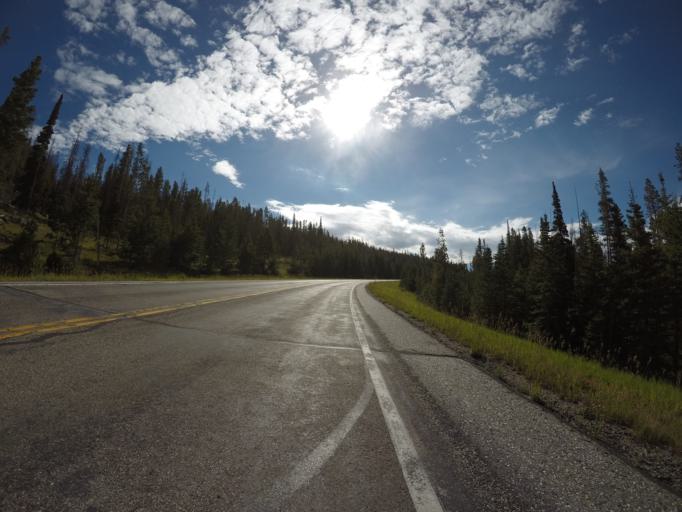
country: US
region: Wyoming
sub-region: Carbon County
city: Saratoga
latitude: 41.3296
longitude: -106.4782
